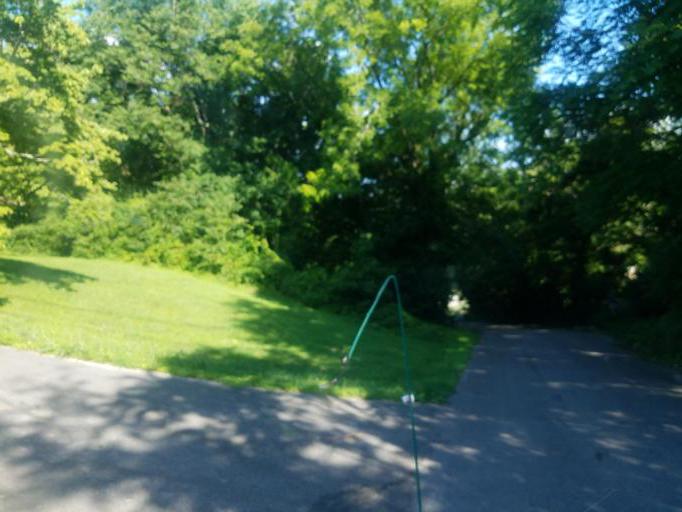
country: US
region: Kentucky
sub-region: Hart County
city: Munfordville
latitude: 37.2698
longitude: -85.8888
